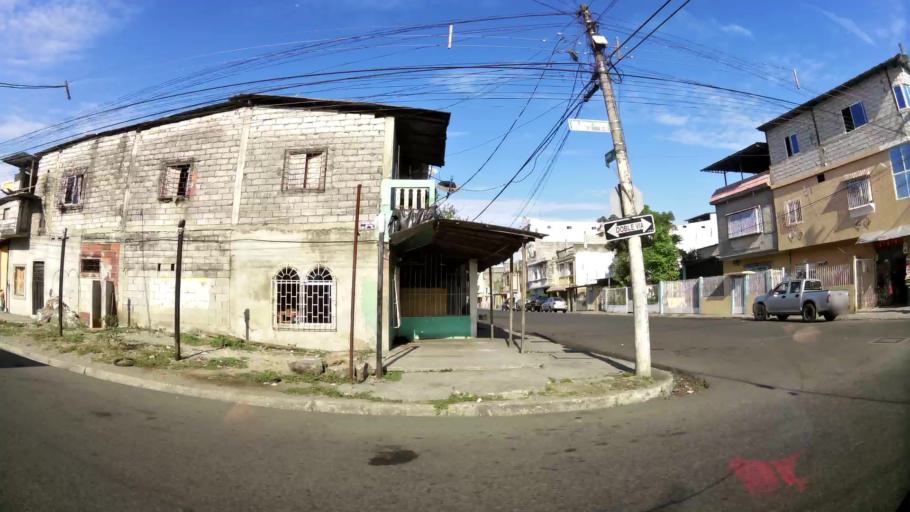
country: EC
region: Guayas
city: Guayaquil
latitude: -2.2180
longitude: -79.9285
